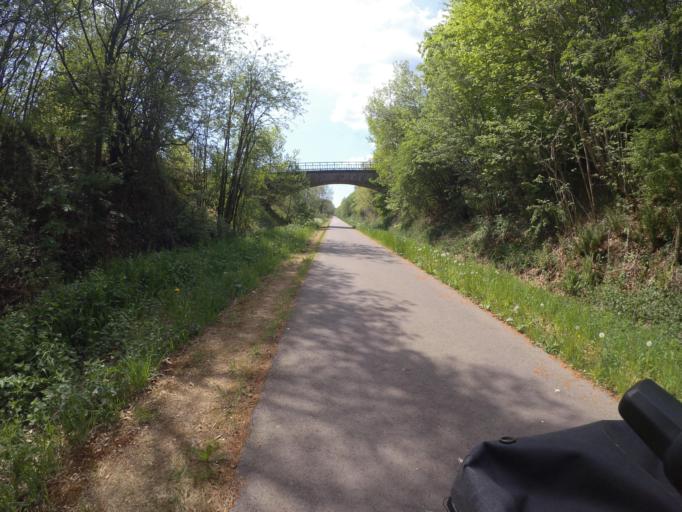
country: BE
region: Wallonia
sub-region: Province de Liege
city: Bullange
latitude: 50.4036
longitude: 6.2684
